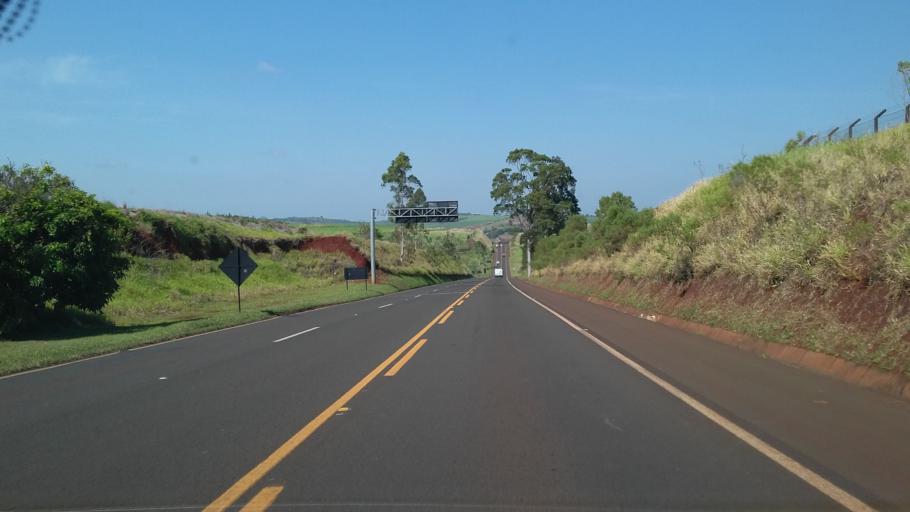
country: BR
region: Parana
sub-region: Bandeirantes
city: Bandeirantes
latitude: -23.1259
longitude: -50.3599
